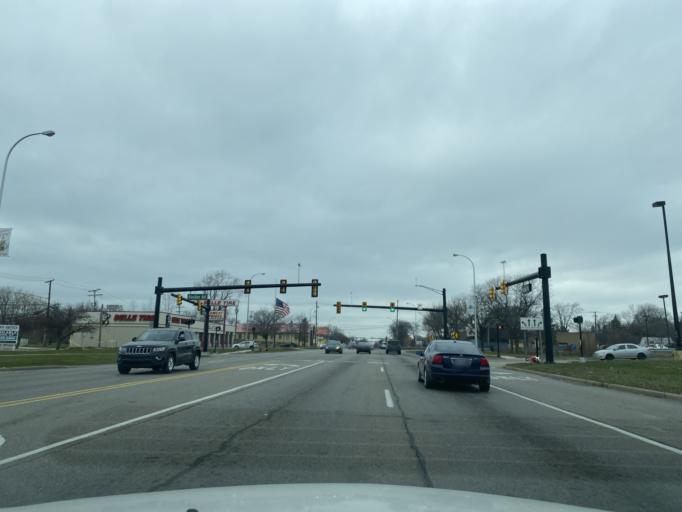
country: US
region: Michigan
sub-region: Wayne County
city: Taylor
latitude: 42.1978
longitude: -83.2610
